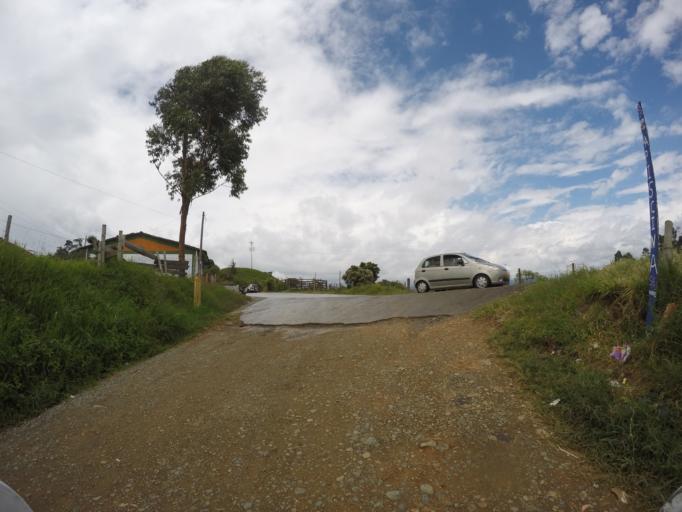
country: CO
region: Quindio
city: Filandia
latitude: 4.6647
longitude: -75.6712
